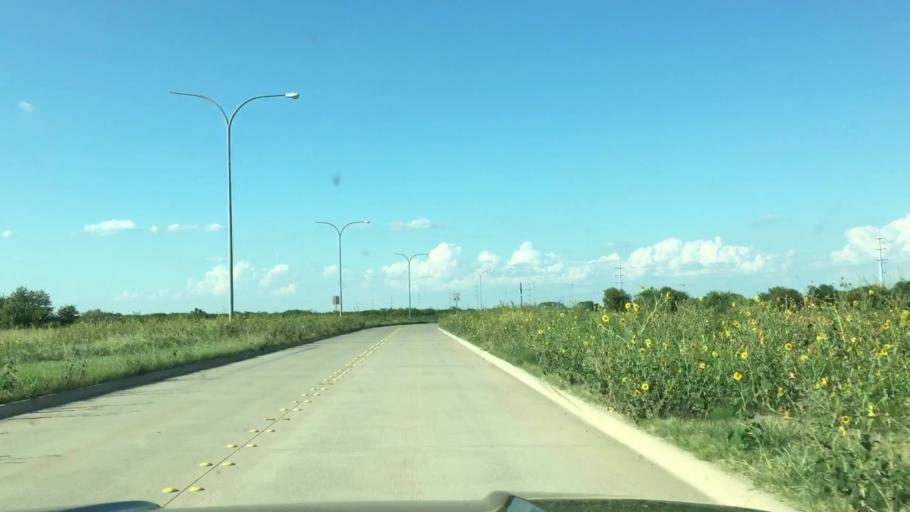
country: US
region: Texas
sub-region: Tarrant County
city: Haslet
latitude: 33.0060
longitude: -97.3584
